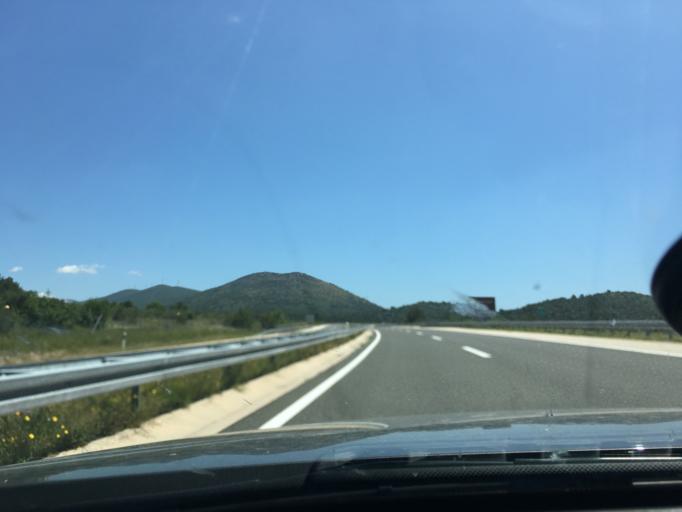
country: HR
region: Sibensko-Kniniska
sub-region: Grad Sibenik
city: Sibenik
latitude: 43.7967
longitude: 15.9173
